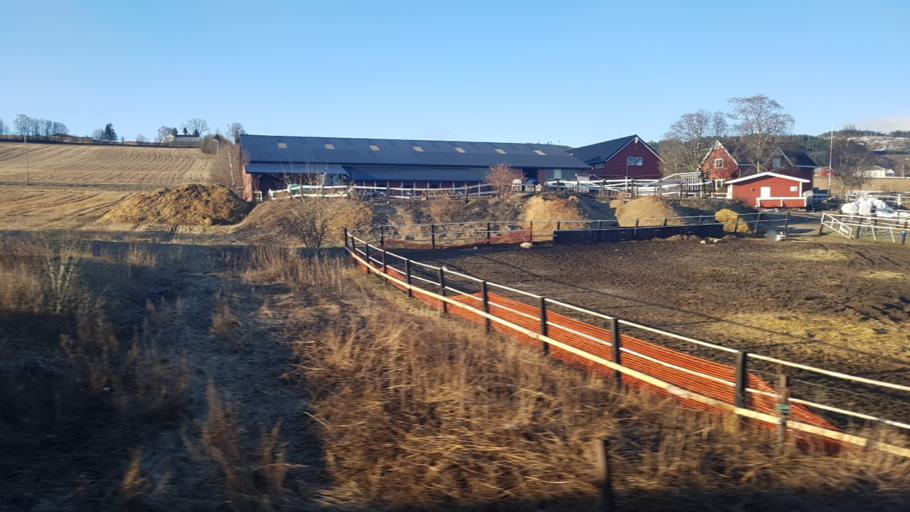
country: NO
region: Sor-Trondelag
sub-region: Malvik
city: Malvik
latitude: 63.4307
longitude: 10.6944
